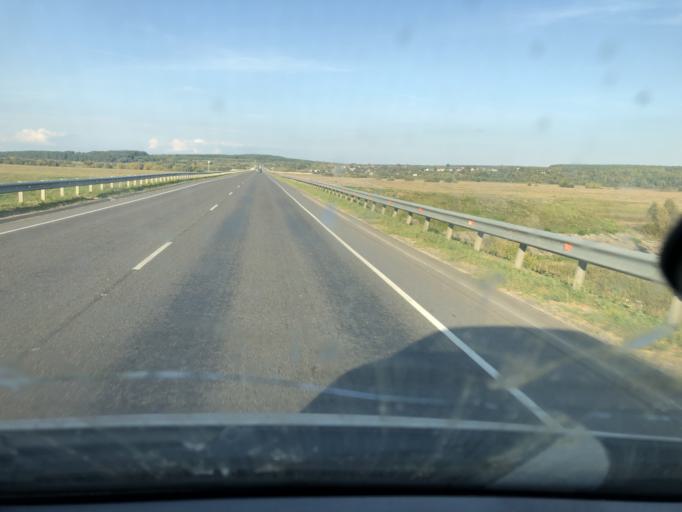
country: RU
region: Kaluga
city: Peremyshl'
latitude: 54.2846
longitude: 36.1577
